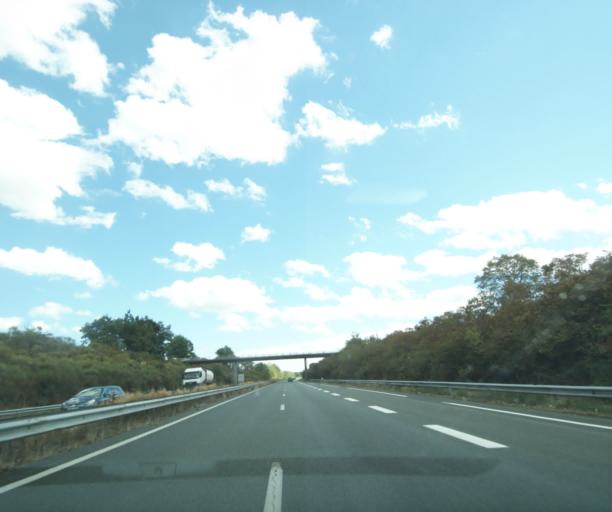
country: FR
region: Aquitaine
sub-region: Departement du Lot-et-Garonne
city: Meilhan-sur-Garonne
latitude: 44.4738
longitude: 0.0431
